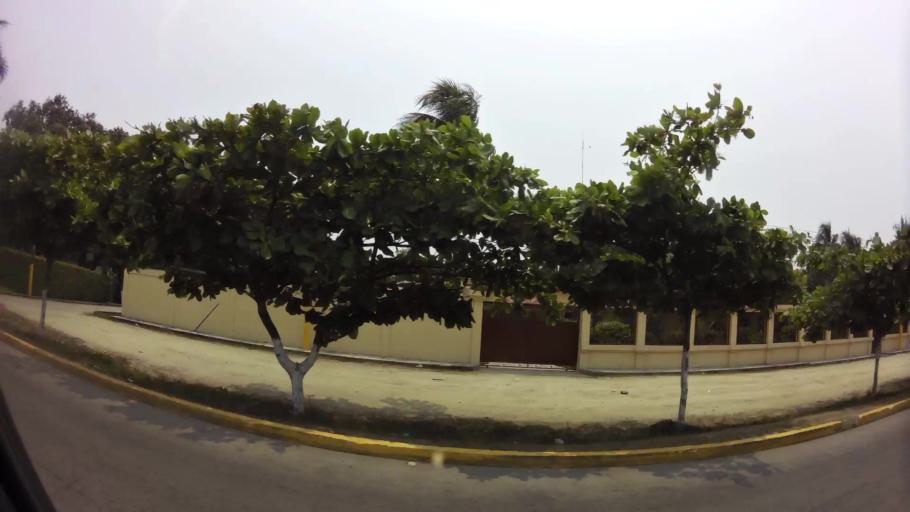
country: HN
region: Yoro
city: El Progreso
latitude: 15.3981
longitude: -87.8130
